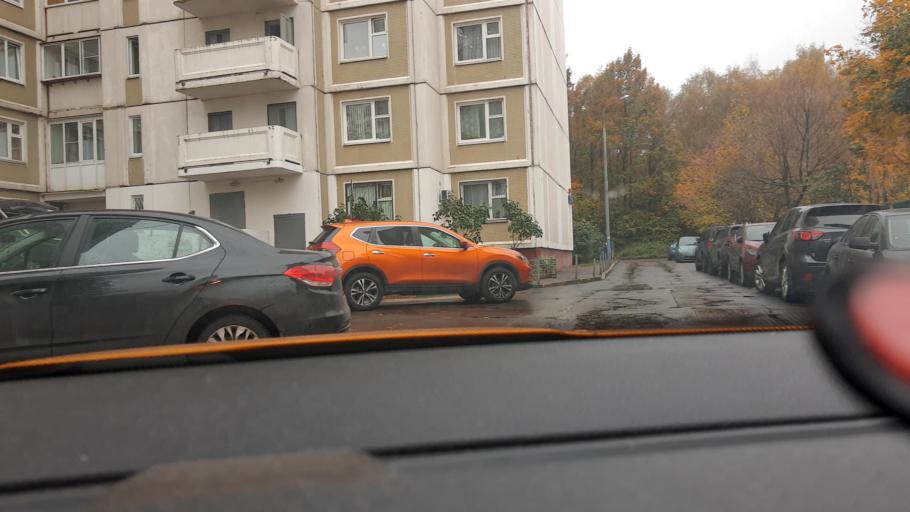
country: RU
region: Moskovskaya
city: Krasnogorsk
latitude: 55.8453
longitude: 37.3431
